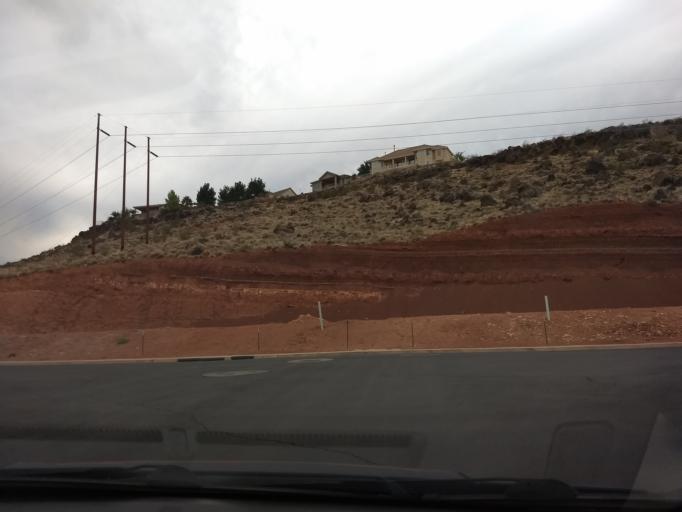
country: US
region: Utah
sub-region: Washington County
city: Saint George
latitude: 37.1043
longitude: -113.5435
